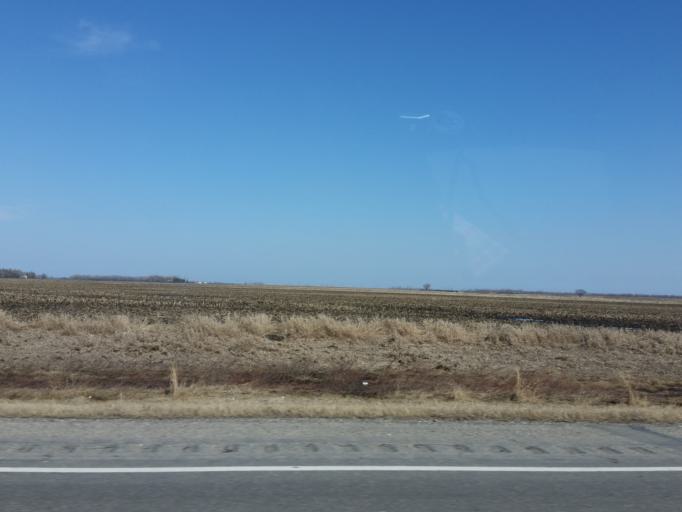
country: US
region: North Dakota
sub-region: Walsh County
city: Grafton
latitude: 48.1987
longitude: -97.3337
